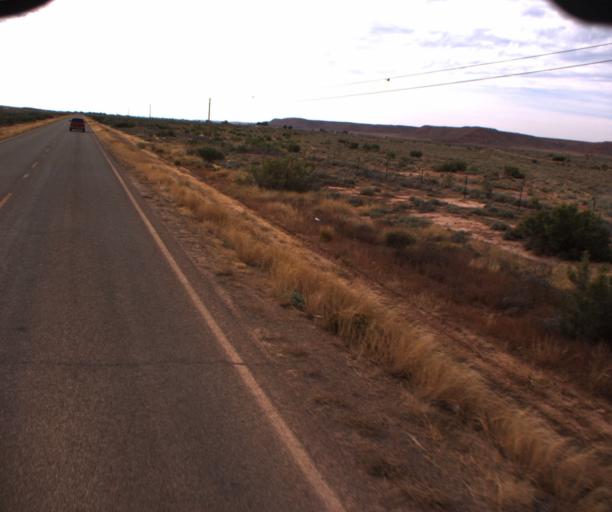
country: US
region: Arizona
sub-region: Apache County
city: Many Farms
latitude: 36.3021
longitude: -109.6077
